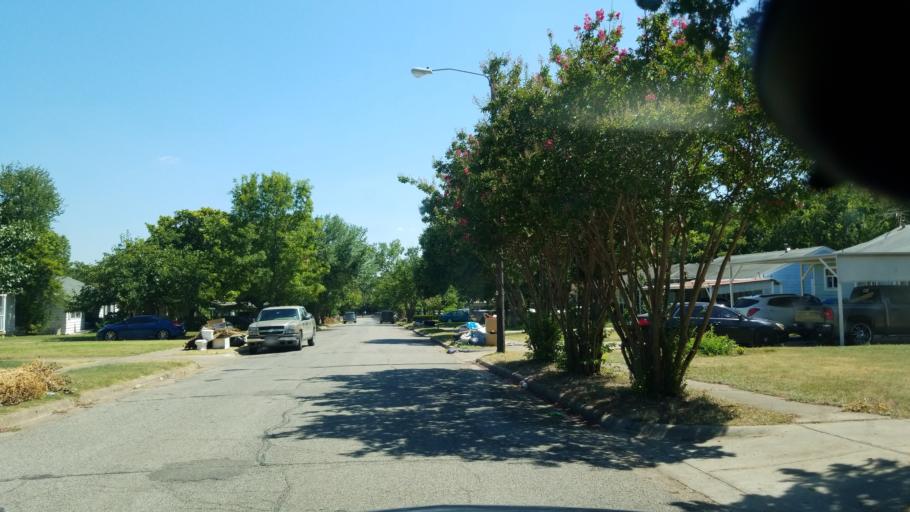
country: US
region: Texas
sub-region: Dallas County
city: Cockrell Hill
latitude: 32.7306
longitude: -96.8518
